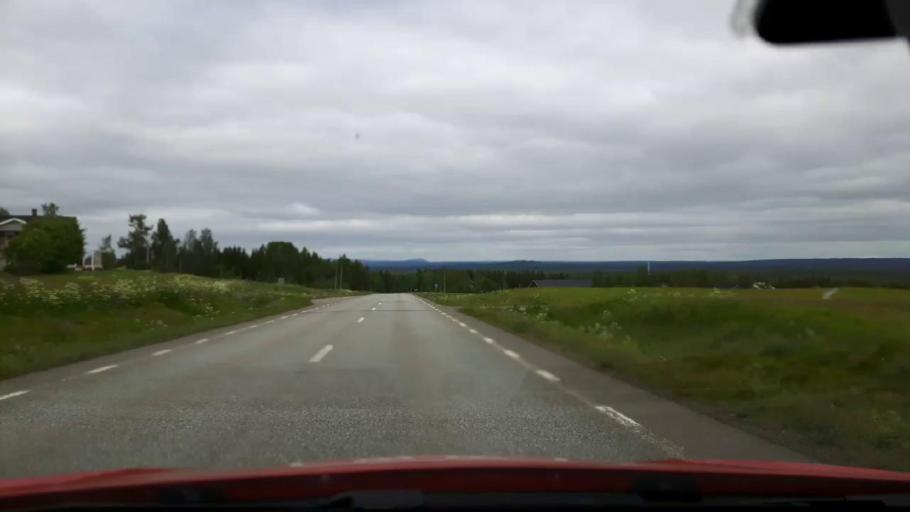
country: SE
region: Jaemtland
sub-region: Krokoms Kommun
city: Krokom
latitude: 63.5811
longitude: 14.6344
